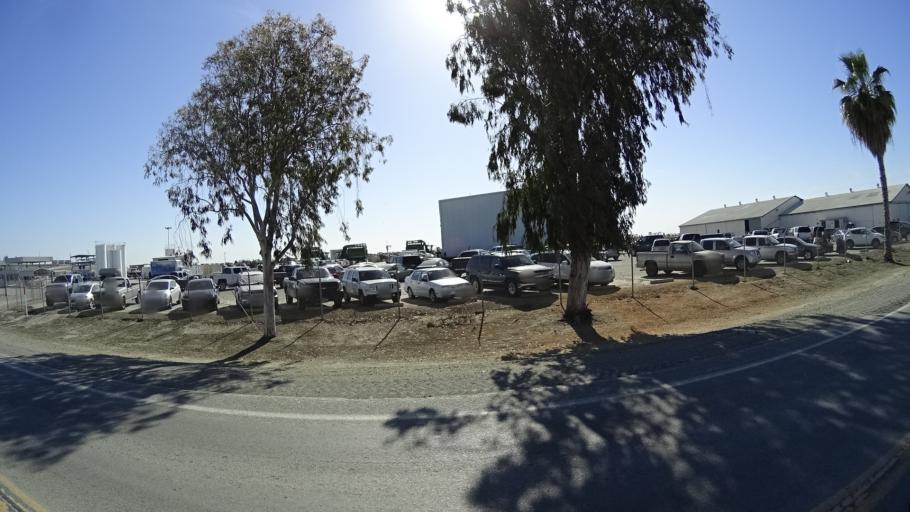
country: US
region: California
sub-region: Kings County
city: Corcoran
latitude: 36.0640
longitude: -119.5720
